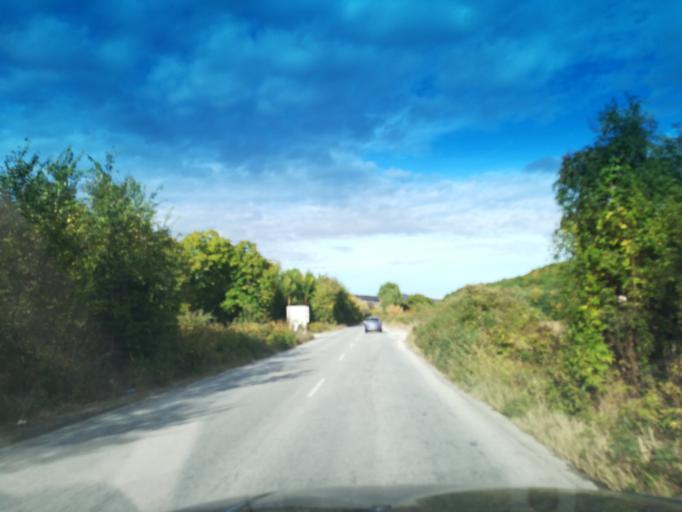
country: BG
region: Pazardzhik
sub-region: Obshtina Bratsigovo
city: Bratsigovo
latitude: 42.0548
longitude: 24.3433
